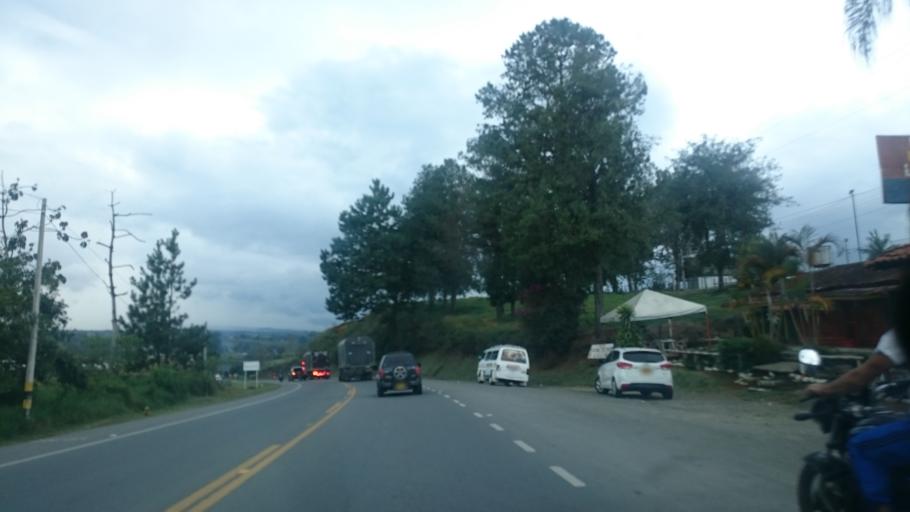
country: CO
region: Cauca
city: Cajibio
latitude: 2.5625
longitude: -76.5640
